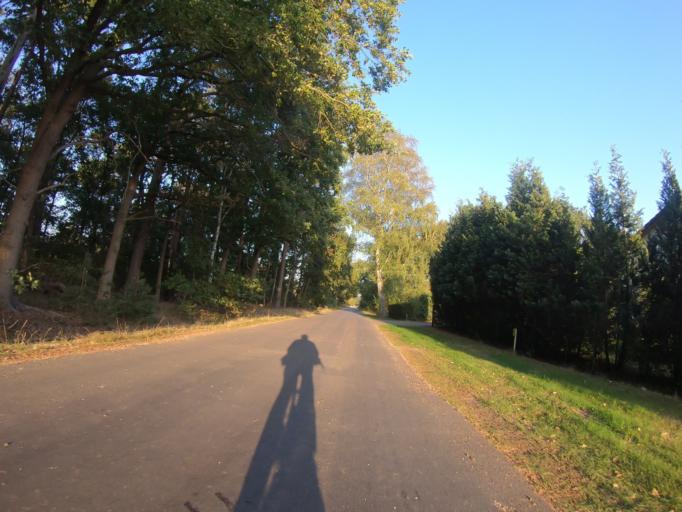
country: DE
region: Lower Saxony
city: Isenbuttel
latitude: 52.4698
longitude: 10.6123
